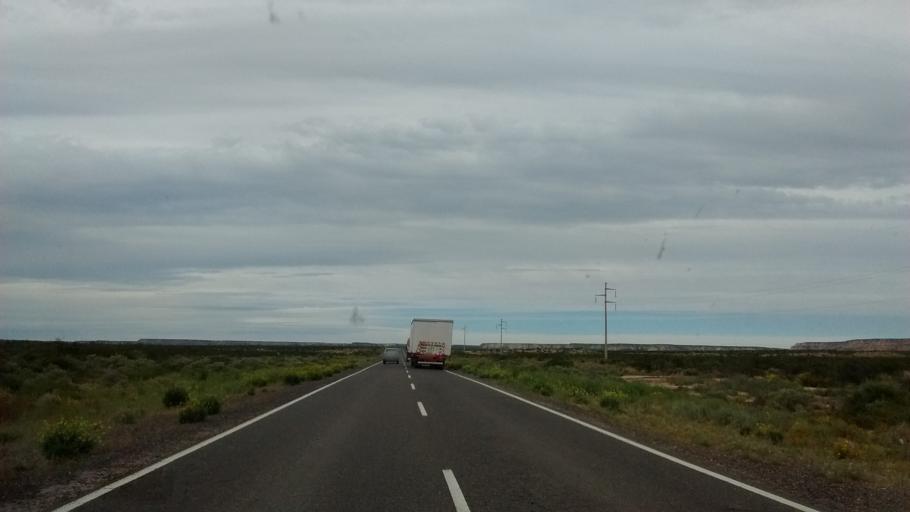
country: AR
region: Rio Negro
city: Catriel
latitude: -38.1377
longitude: -67.9376
